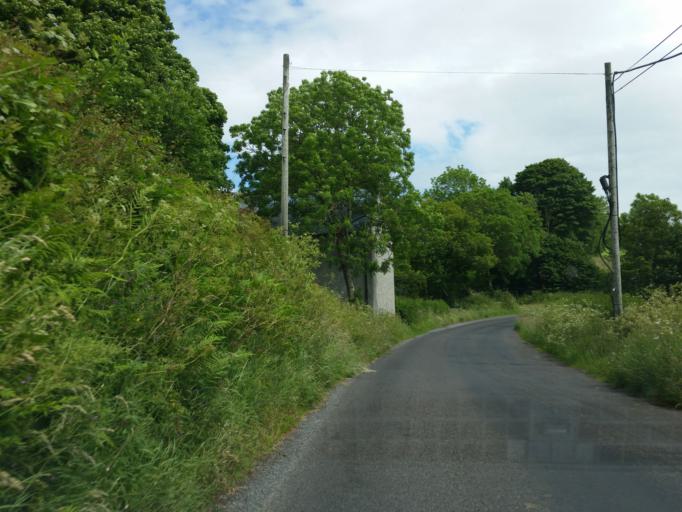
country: GB
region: Northern Ireland
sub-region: Omagh District
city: Omagh
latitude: 54.5491
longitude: -7.0926
